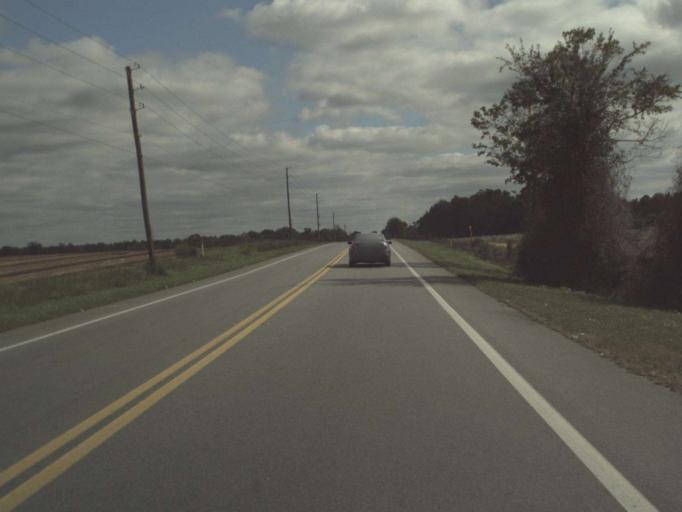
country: US
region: Florida
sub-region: Jackson County
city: Marianna
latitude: 30.6657
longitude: -85.1667
